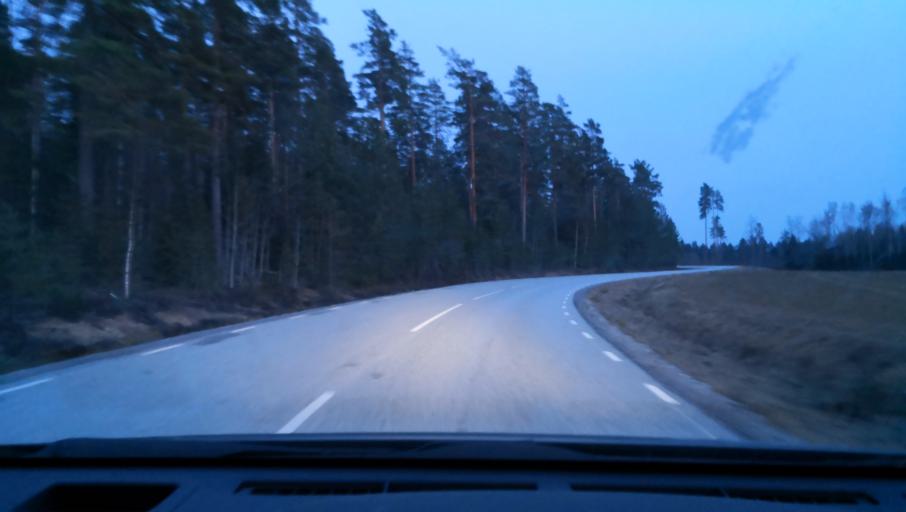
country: SE
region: OErebro
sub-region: Lindesbergs Kommun
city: Frovi
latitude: 59.5880
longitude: 15.4377
